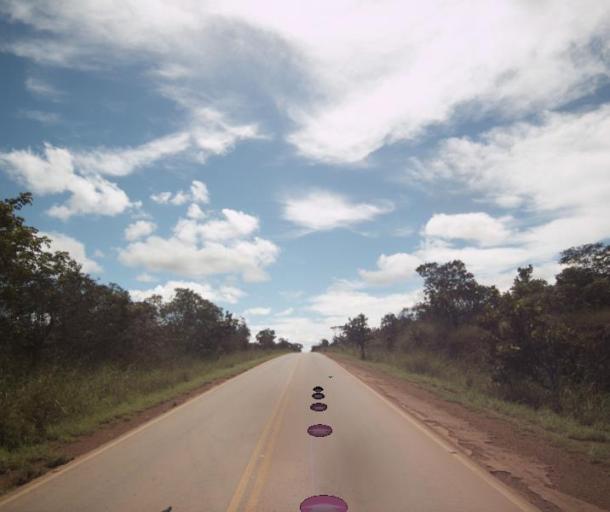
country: BR
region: Goias
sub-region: Padre Bernardo
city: Padre Bernardo
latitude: -15.4099
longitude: -48.2004
